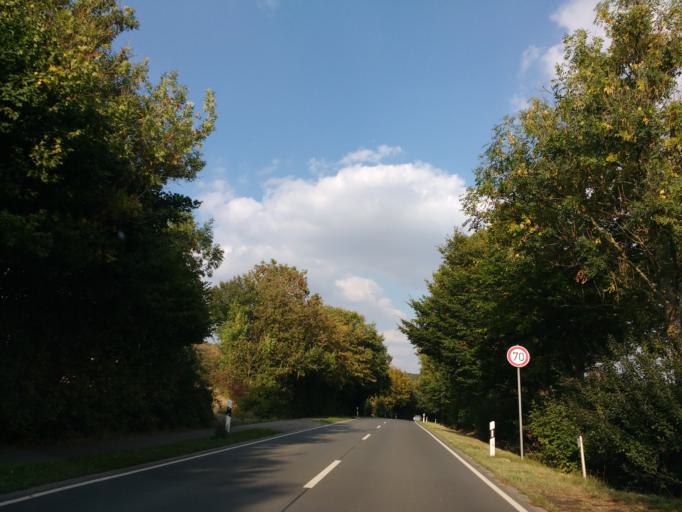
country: DE
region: North Rhine-Westphalia
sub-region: Regierungsbezirk Detmold
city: Blomberg
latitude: 51.9448
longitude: 9.0354
